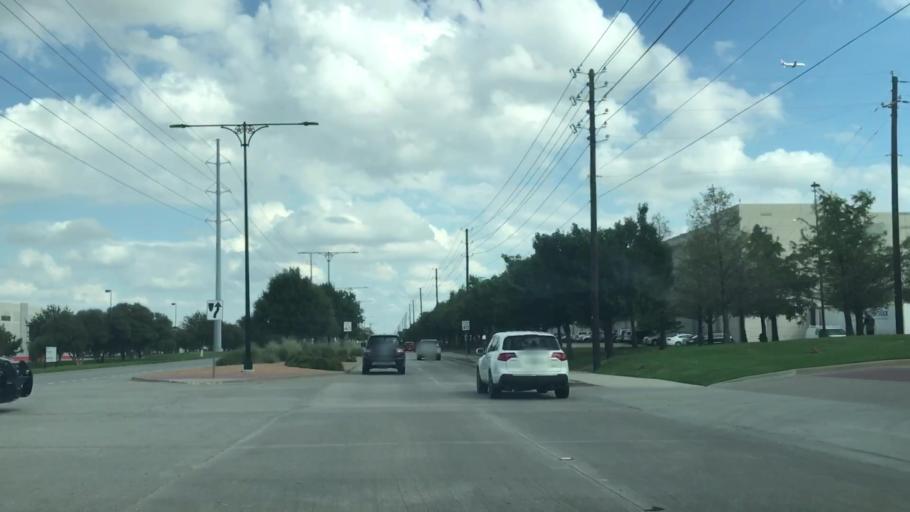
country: US
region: Texas
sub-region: Dallas County
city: Coppell
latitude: 32.9728
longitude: -97.0232
